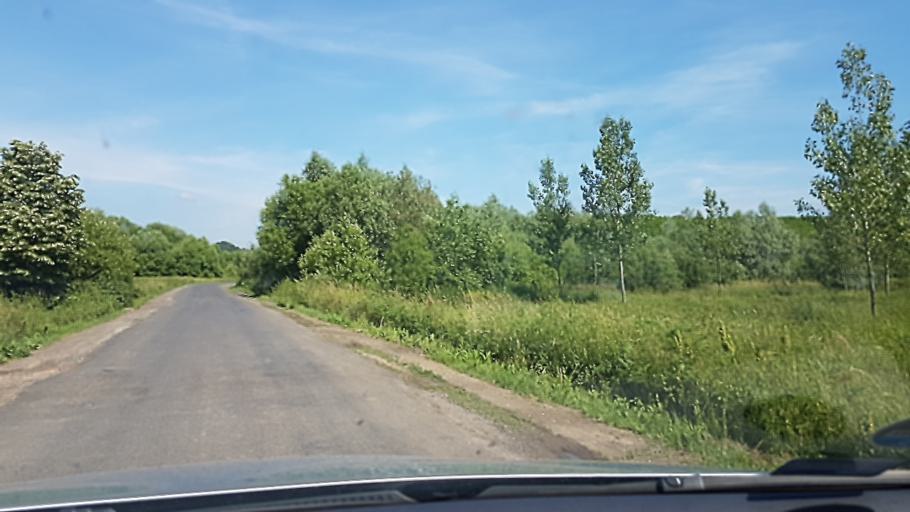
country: HU
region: Borsod-Abauj-Zemplen
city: Saly
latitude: 47.9403
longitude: 20.7086
